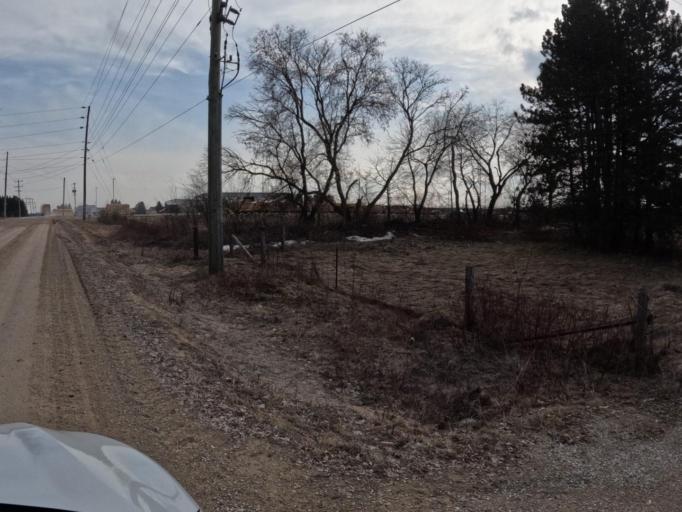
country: CA
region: Ontario
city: Shelburne
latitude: 43.9056
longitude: -80.3026
